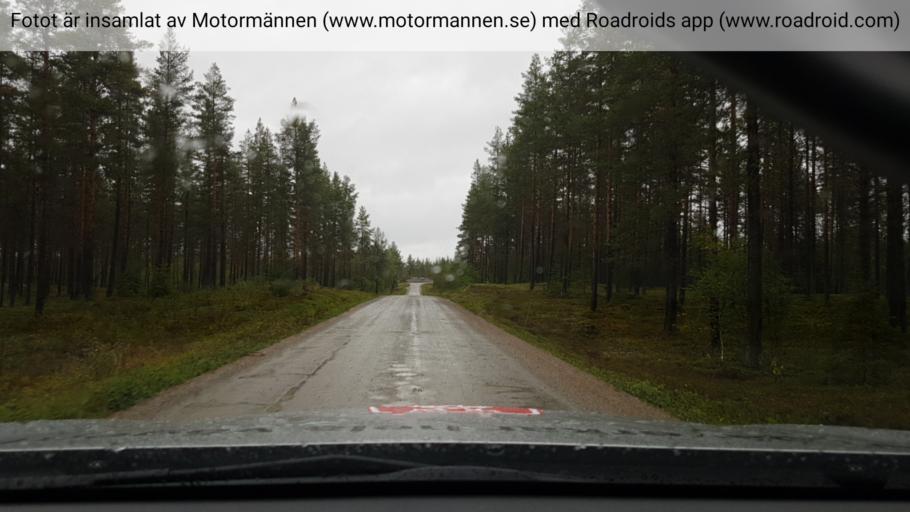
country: SE
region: Vaesterbotten
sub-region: Asele Kommun
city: Asele
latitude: 64.0541
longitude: 17.6368
